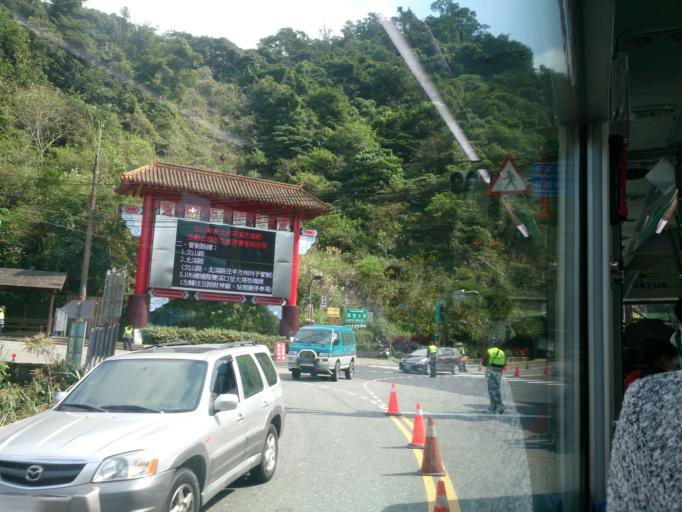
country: TW
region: Taipei
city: Taipei
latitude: 25.0064
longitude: 121.6516
